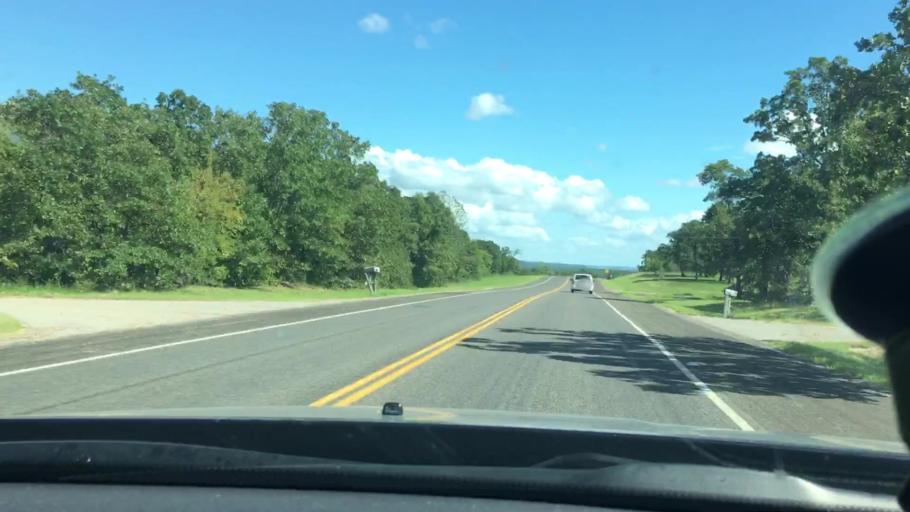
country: US
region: Oklahoma
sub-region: Sequoyah County
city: Vian
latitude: 35.5536
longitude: -94.9747
